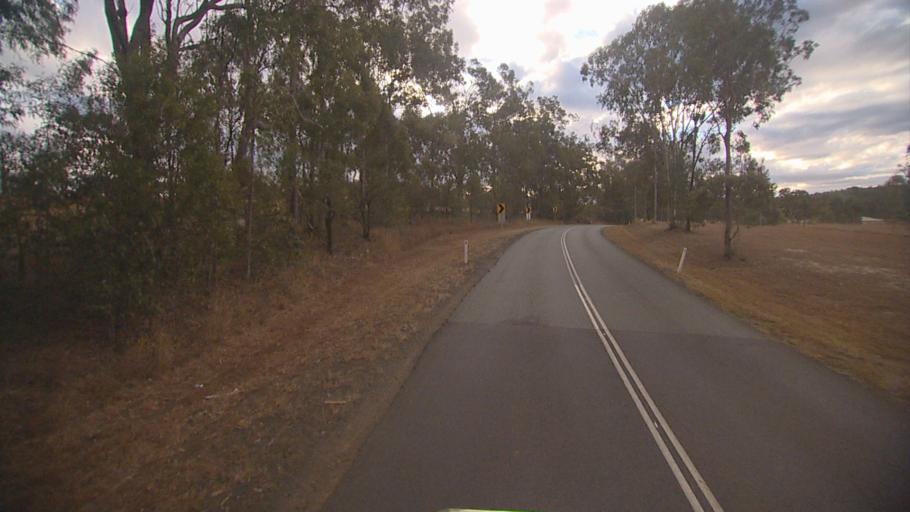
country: AU
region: Queensland
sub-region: Logan
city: Cedar Vale
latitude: -27.8819
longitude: 153.0712
